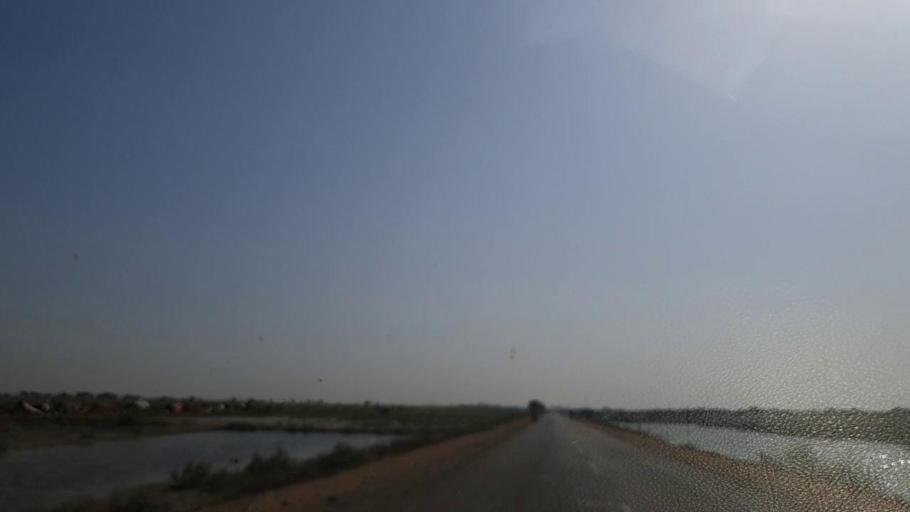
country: PK
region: Sindh
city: Jati
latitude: 24.5382
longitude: 68.2793
